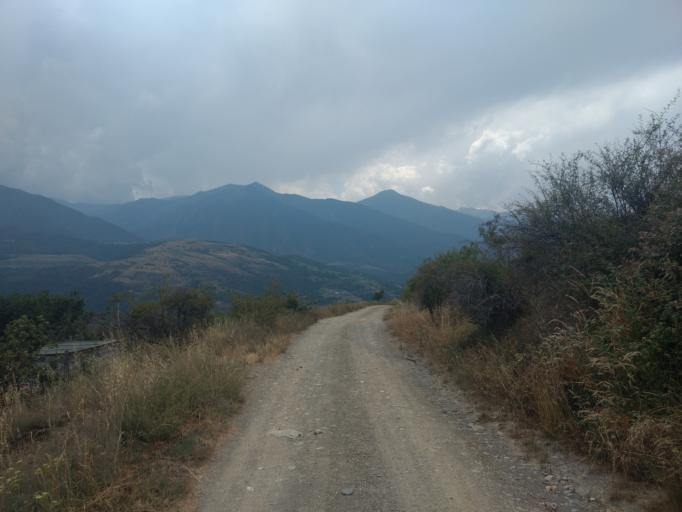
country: FR
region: Languedoc-Roussillon
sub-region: Departement des Pyrenees-Orientales
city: Vernet-les-Bains
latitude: 42.5715
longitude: 2.2941
